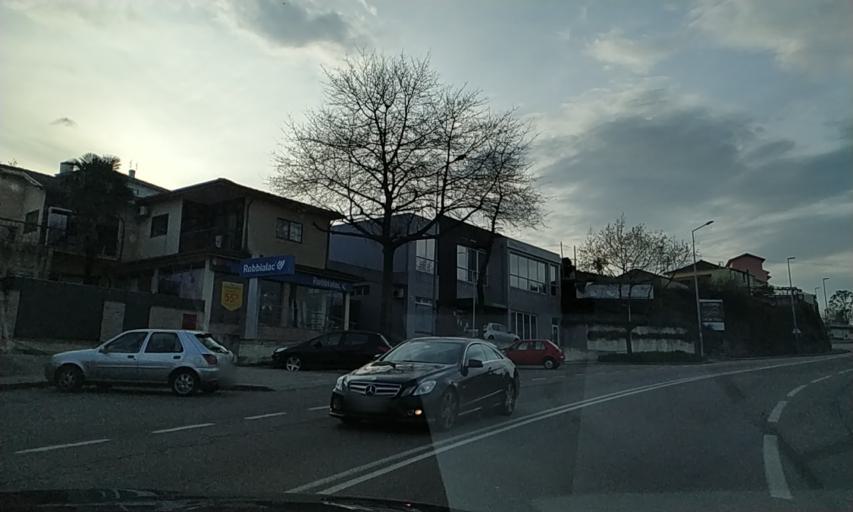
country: PT
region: Porto
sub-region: Valongo
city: Valongo
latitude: 41.1904
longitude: -8.5062
